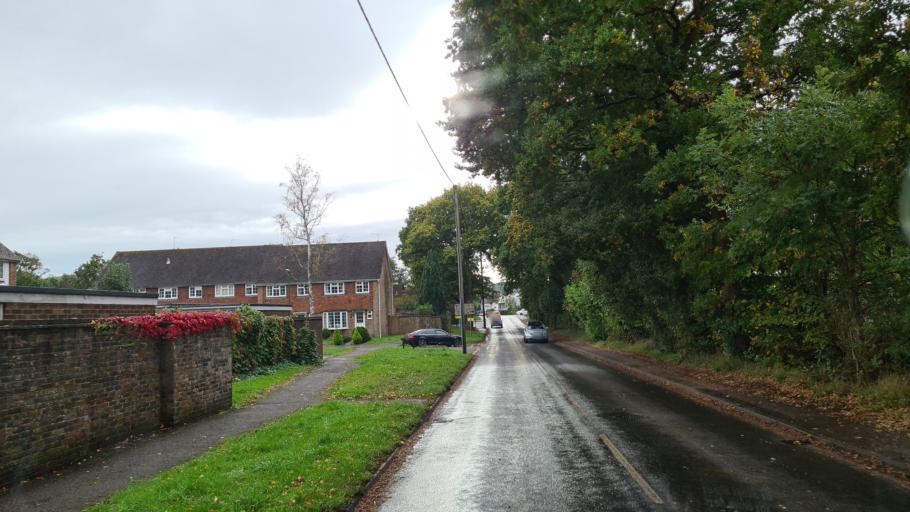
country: GB
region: England
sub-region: West Sussex
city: Storrington
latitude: 50.9206
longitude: -0.4473
